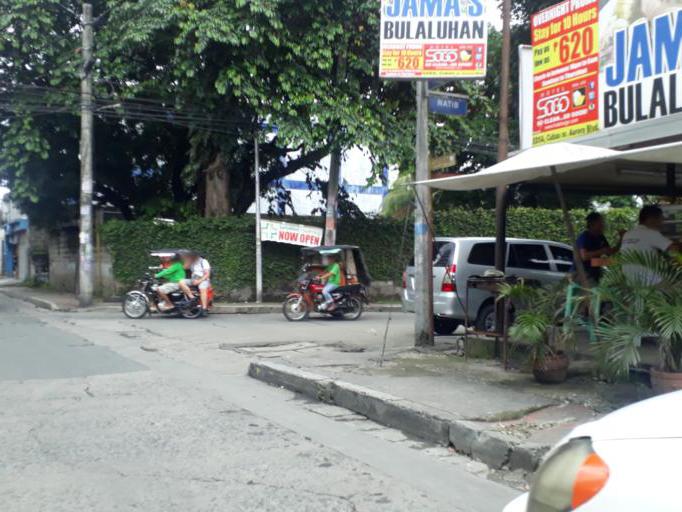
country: PH
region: Metro Manila
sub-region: San Juan
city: San Juan
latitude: 14.6171
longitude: 121.0458
